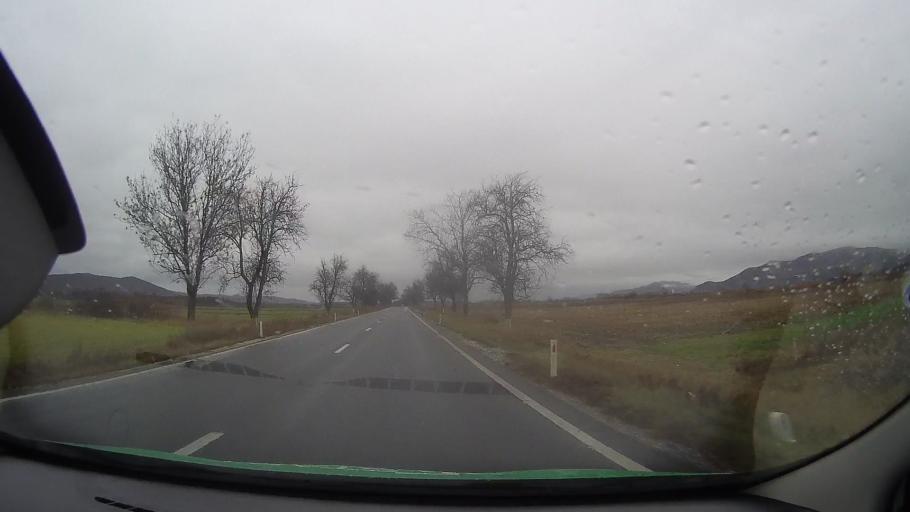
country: RO
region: Mures
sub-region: Comuna Suseni
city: Suseni
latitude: 46.8271
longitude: 24.7395
